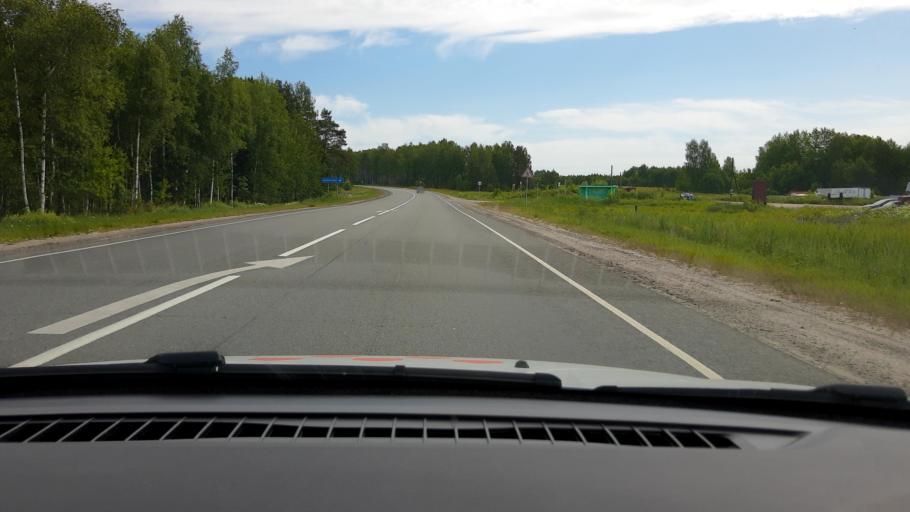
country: RU
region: Nizjnij Novgorod
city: Linda
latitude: 56.6666
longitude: 44.1353
